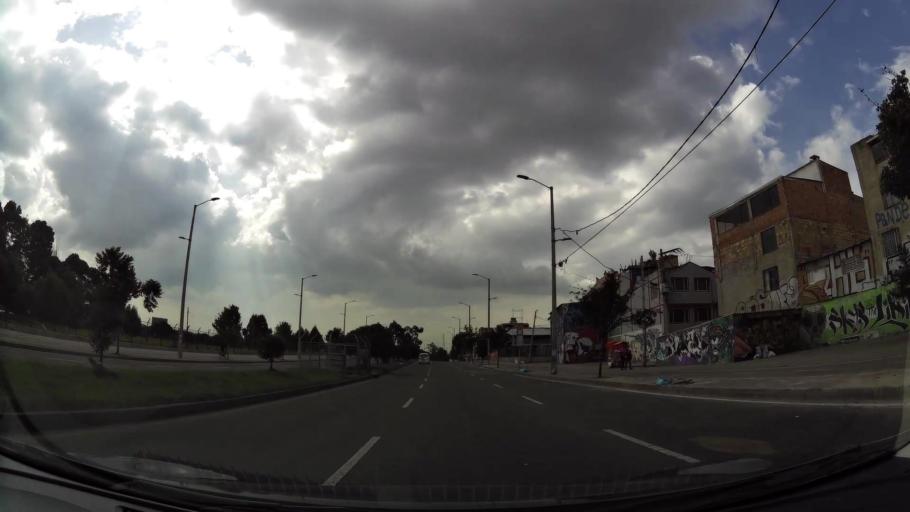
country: CO
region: Cundinamarca
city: Cota
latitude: 4.7208
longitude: -74.0955
